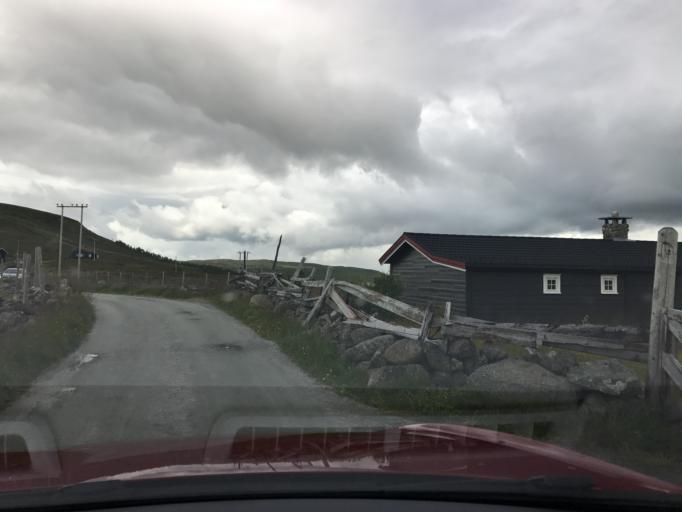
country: NO
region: Buskerud
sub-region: Hol
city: Geilo
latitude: 60.5472
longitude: 8.1807
